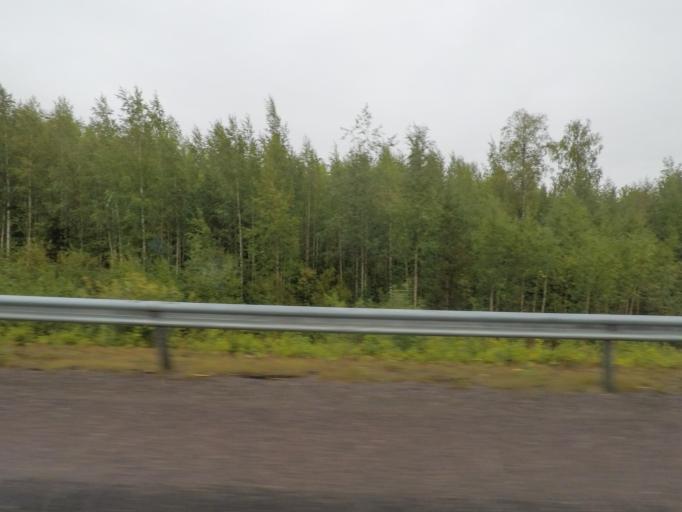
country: FI
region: Northern Savo
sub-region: Varkaus
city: Leppaevirta
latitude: 62.4078
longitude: 27.8260
